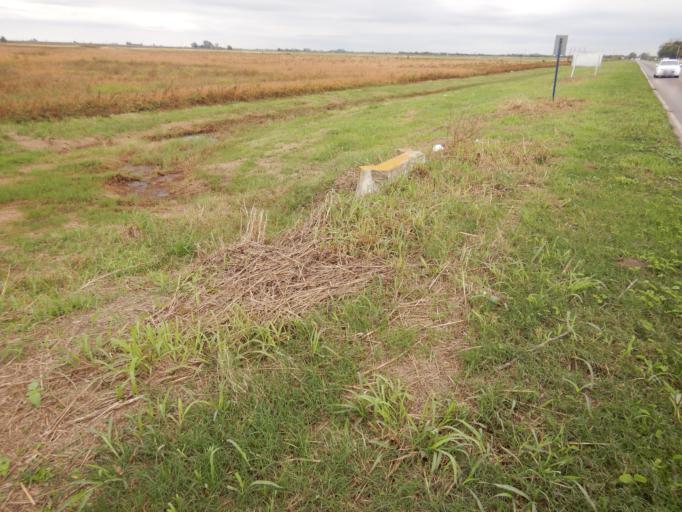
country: AR
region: Santa Fe
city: Roldan
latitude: -32.8918
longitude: -60.9854
